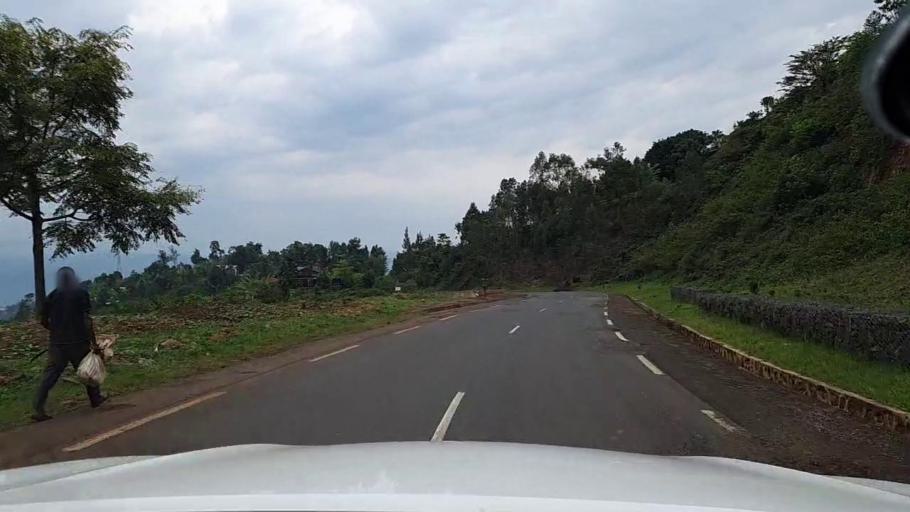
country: RW
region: Western Province
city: Cyangugu
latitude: -2.6564
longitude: 28.9714
